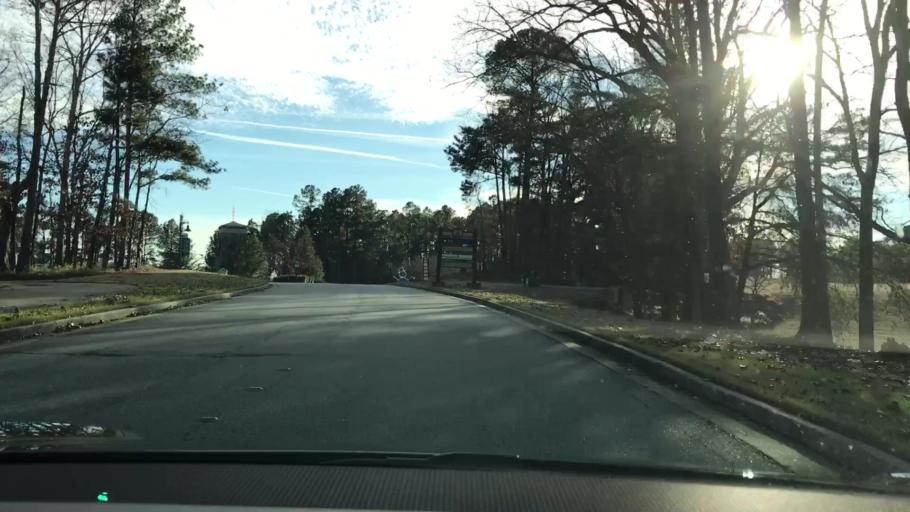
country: US
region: Georgia
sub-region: Gwinnett County
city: Buford
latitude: 34.1793
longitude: -84.0213
